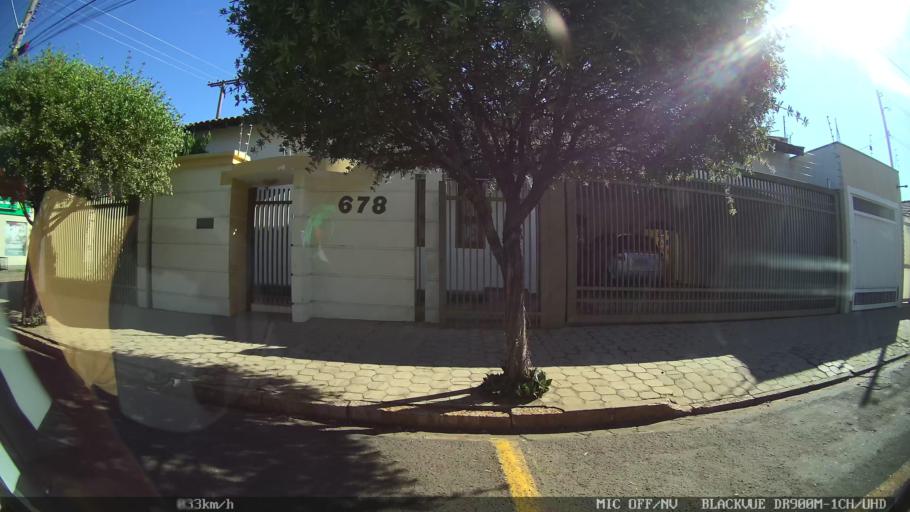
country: BR
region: Sao Paulo
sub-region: Olimpia
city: Olimpia
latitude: -20.7406
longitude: -48.9170
